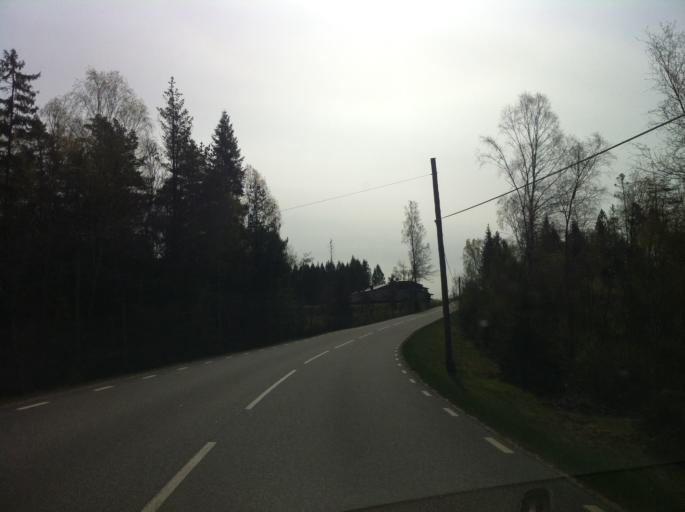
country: SE
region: Vaestra Goetaland
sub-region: Marks Kommun
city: Fritsla
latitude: 57.3525
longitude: 12.8798
